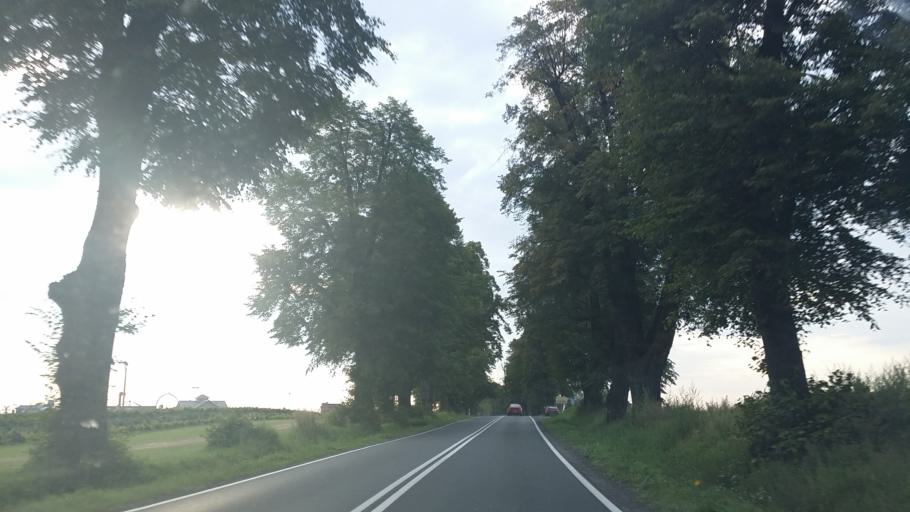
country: PL
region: Lesser Poland Voivodeship
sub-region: Powiat oswiecimski
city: Zator
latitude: 49.9995
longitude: 19.4155
